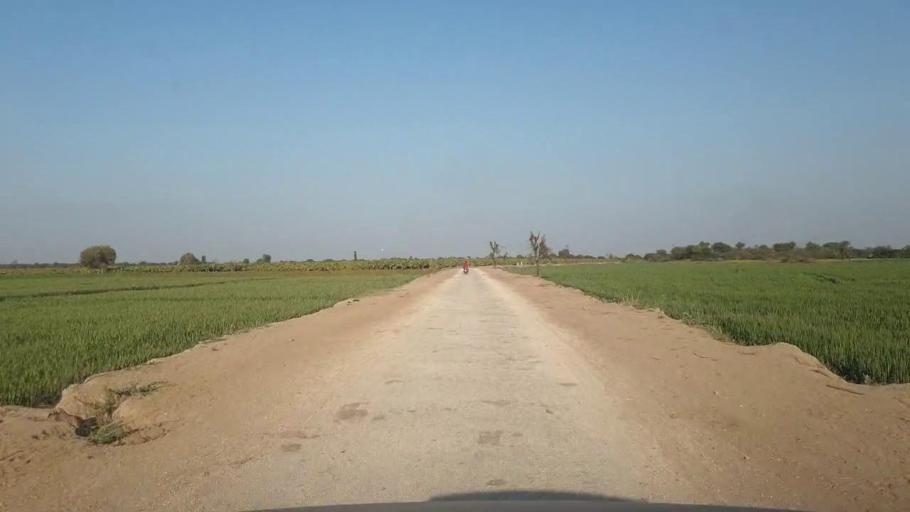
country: PK
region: Sindh
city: Chambar
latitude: 25.2566
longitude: 68.8885
